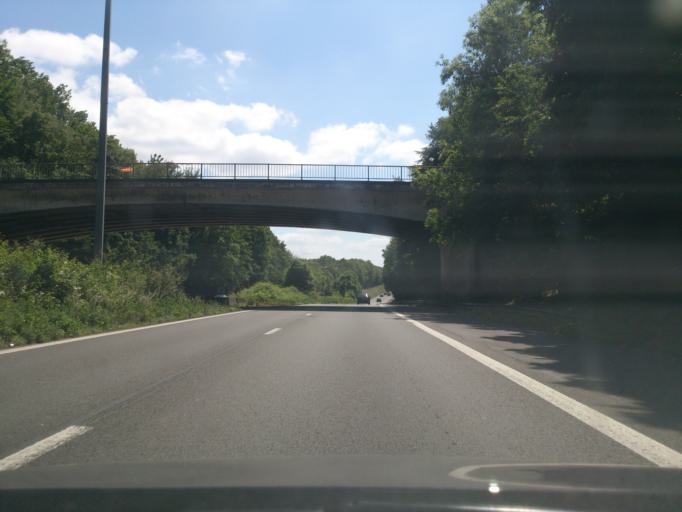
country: BE
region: Wallonia
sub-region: Province du Brabant Wallon
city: Waterloo
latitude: 50.7154
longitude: 4.4126
